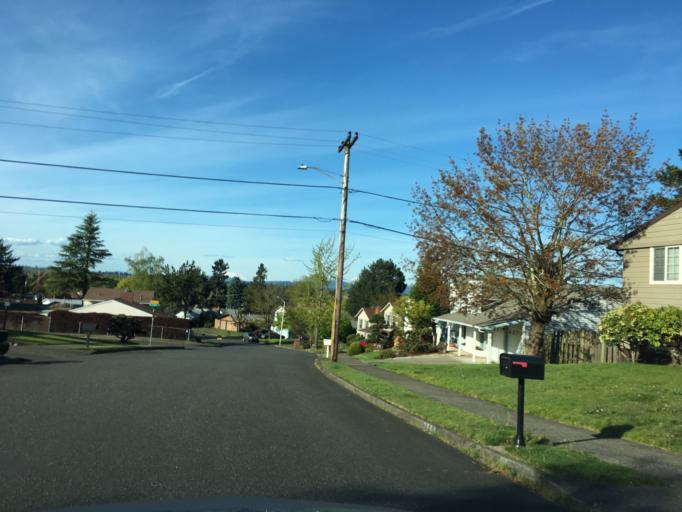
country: US
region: Oregon
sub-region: Multnomah County
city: Lents
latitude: 45.5509
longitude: -122.5256
